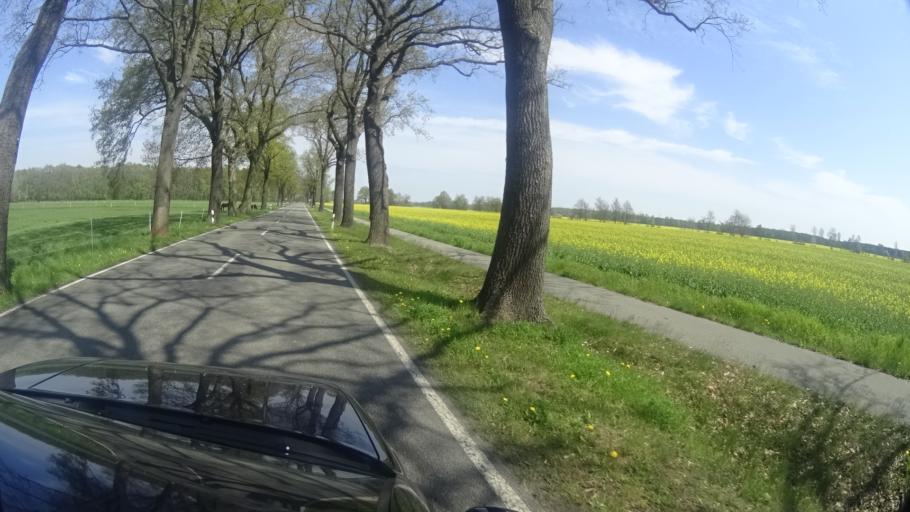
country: DE
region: Brandenburg
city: Dreetz
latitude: 52.8299
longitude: 12.4282
